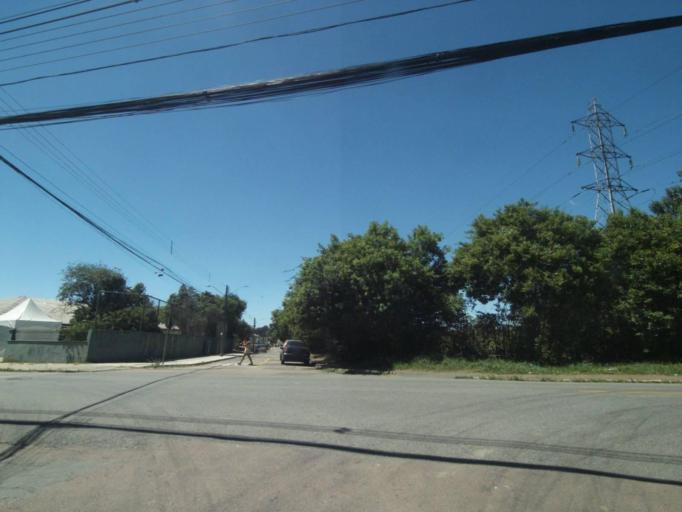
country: BR
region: Parana
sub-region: Curitiba
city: Curitiba
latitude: -25.4749
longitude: -49.3438
